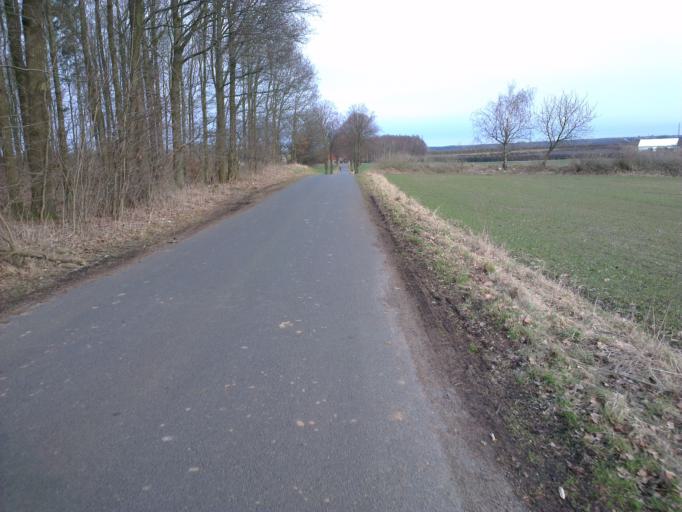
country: DK
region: Capital Region
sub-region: Frederikssund Kommune
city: Skibby
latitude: 55.7901
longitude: 11.9619
